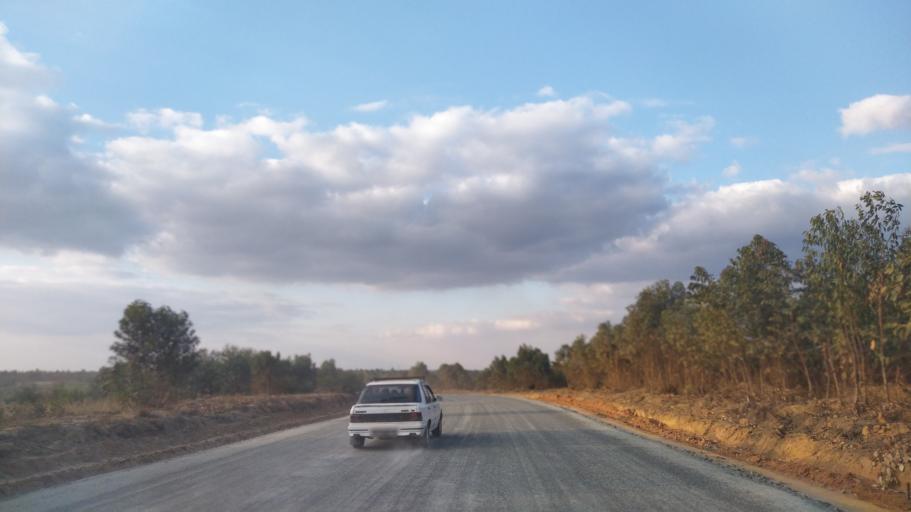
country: MG
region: Analamanga
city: Anjozorobe
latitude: -18.4874
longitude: 48.2653
